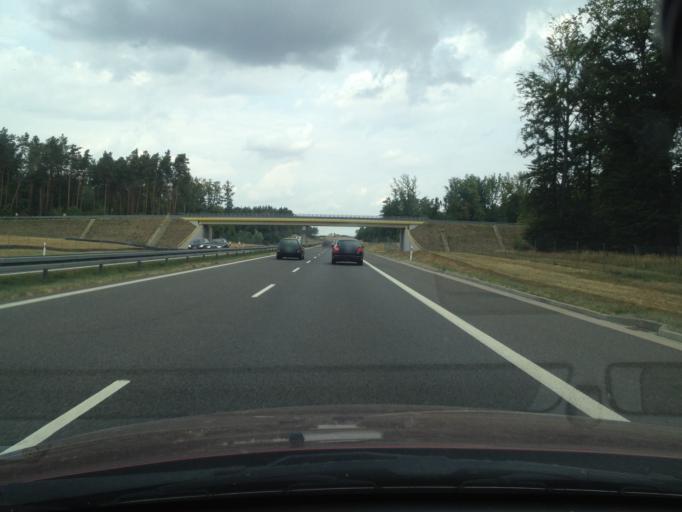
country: PL
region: West Pomeranian Voivodeship
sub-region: Powiat mysliborski
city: Mysliborz
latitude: 53.0103
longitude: 14.8619
